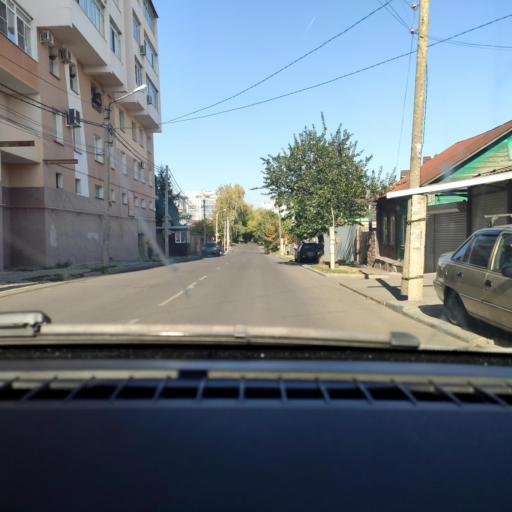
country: RU
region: Voronezj
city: Voronezh
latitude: 51.6657
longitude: 39.2146
